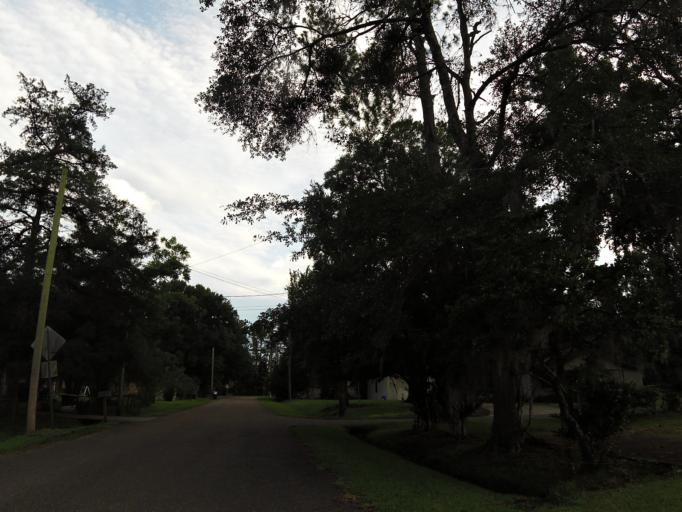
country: US
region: Florida
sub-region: Duval County
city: Jacksonville
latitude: 30.3247
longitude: -81.7618
